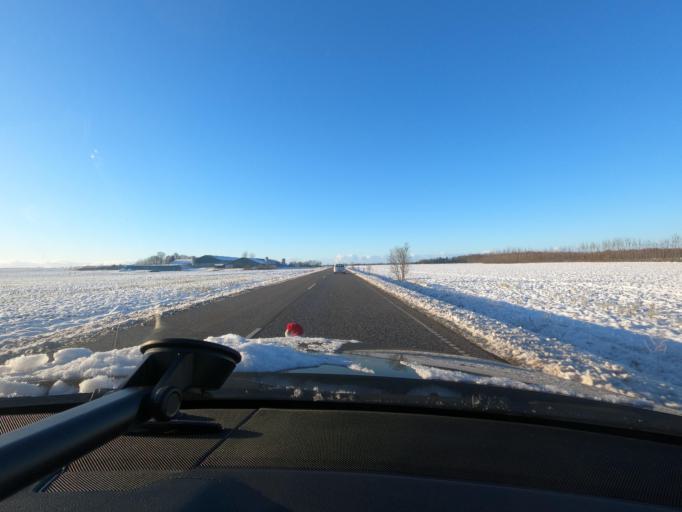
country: DK
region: South Denmark
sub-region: Tonder Kommune
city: Sherrebek
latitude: 55.1770
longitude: 8.8178
